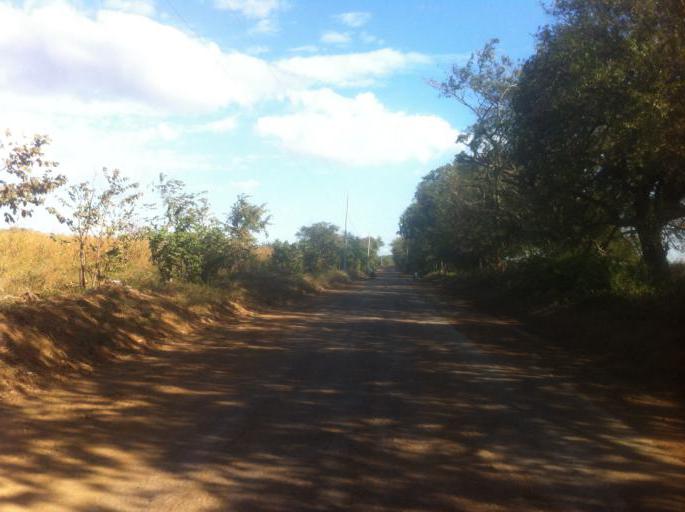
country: NI
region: Managua
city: Masachapa
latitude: 11.8813
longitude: -86.5793
